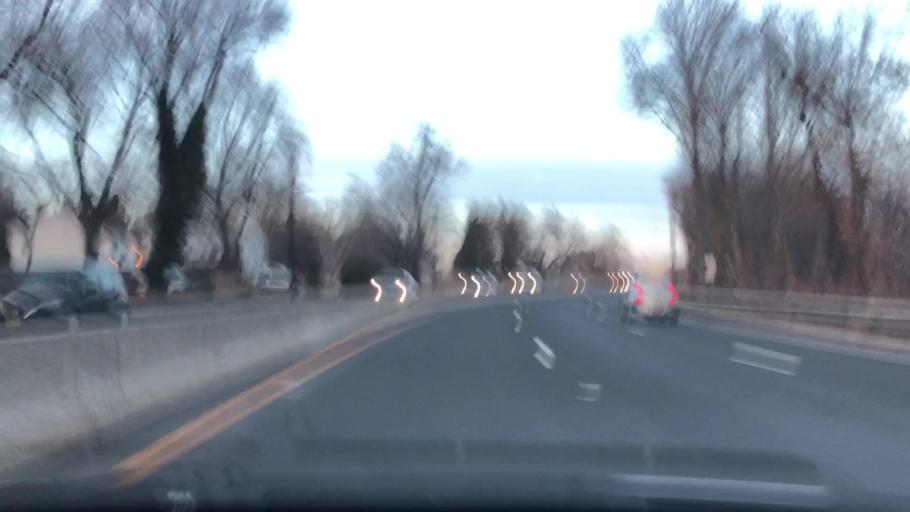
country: US
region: New Jersey
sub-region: Bergen County
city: Elmwood Park
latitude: 40.9131
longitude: -74.1344
